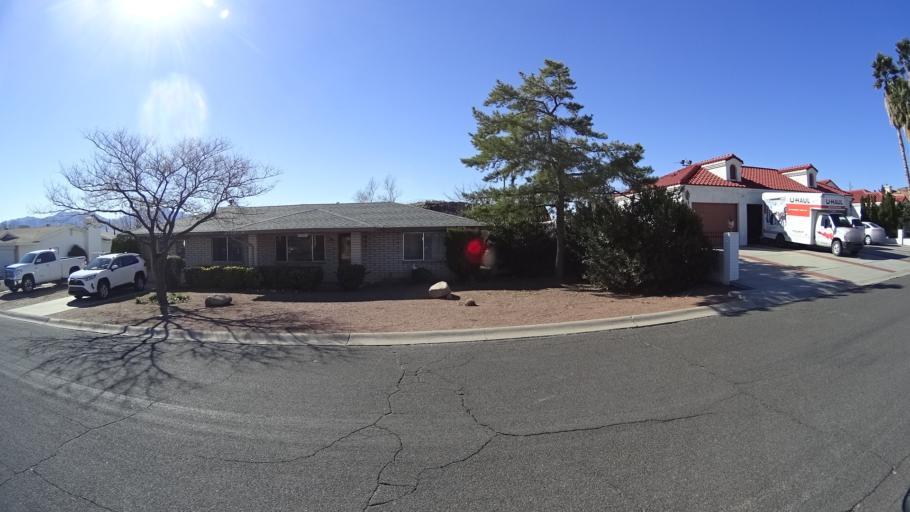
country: US
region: Arizona
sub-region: Mohave County
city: New Kingman-Butler
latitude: 35.2336
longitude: -114.0424
